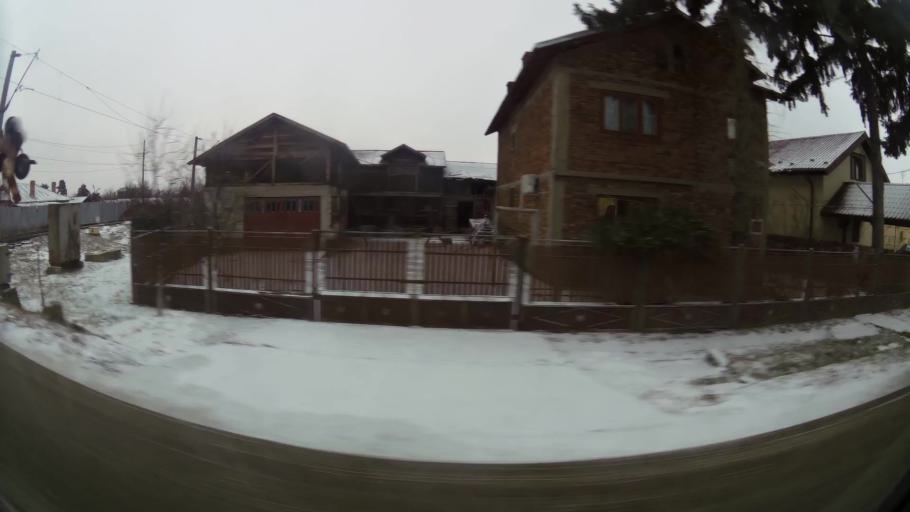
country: RO
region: Prahova
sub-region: Comuna Berceni
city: Corlatesti
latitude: 44.9174
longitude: 26.0827
